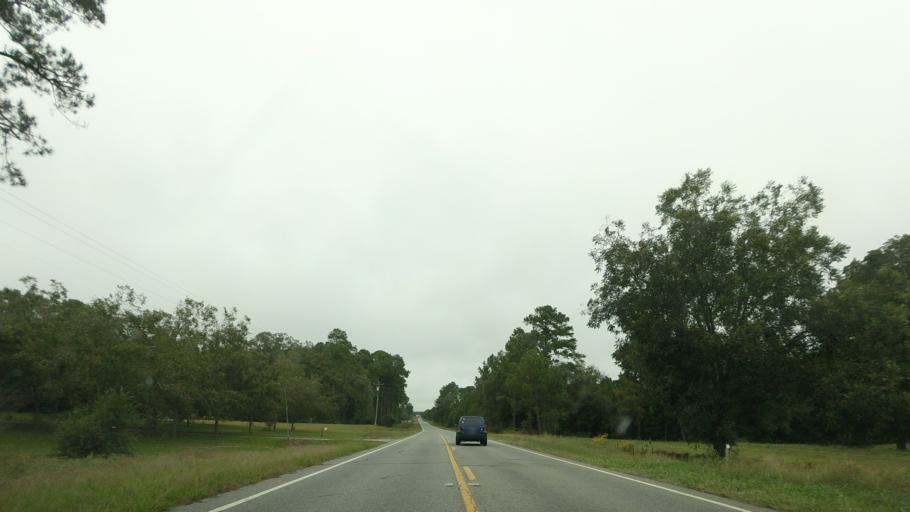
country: US
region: Georgia
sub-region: Irwin County
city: Ocilla
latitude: 31.5608
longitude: -83.2530
